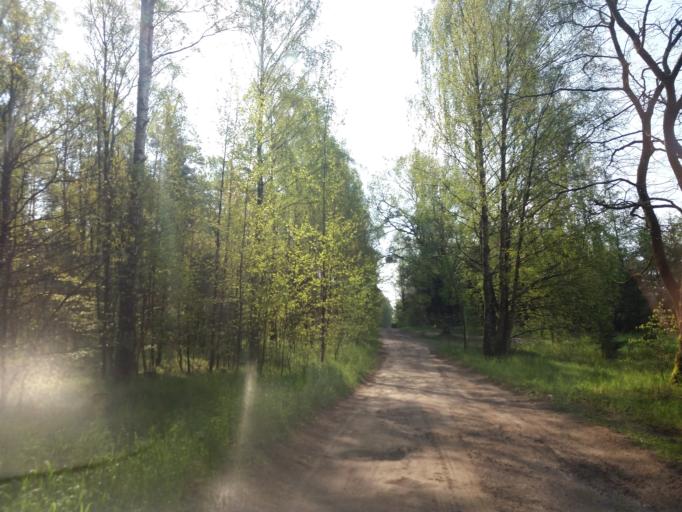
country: PL
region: West Pomeranian Voivodeship
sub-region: Powiat choszczenski
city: Drawno
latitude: 53.2141
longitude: 15.8316
